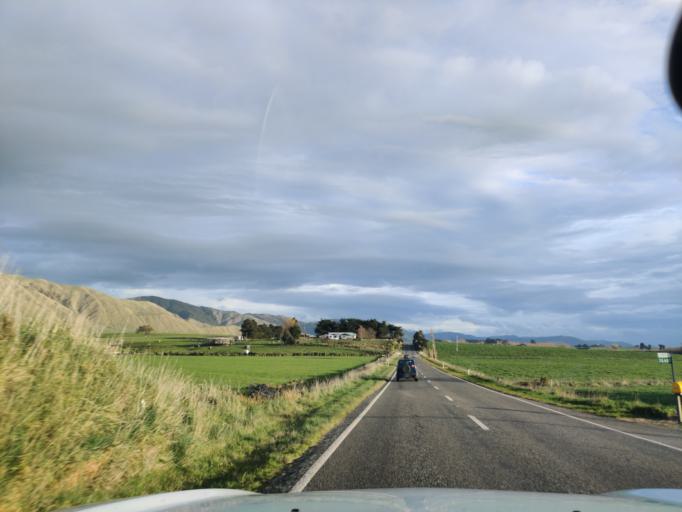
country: NZ
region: Manawatu-Wanganui
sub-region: Horowhenua District
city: Foxton
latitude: -40.5022
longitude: 175.4874
